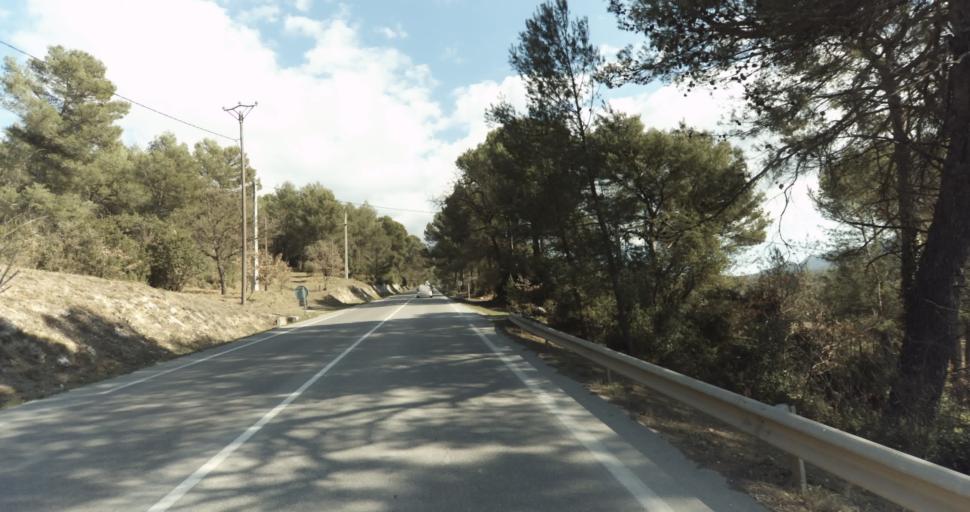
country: FR
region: Provence-Alpes-Cote d'Azur
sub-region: Departement des Bouches-du-Rhone
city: Gardanne
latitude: 43.4510
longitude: 5.4988
